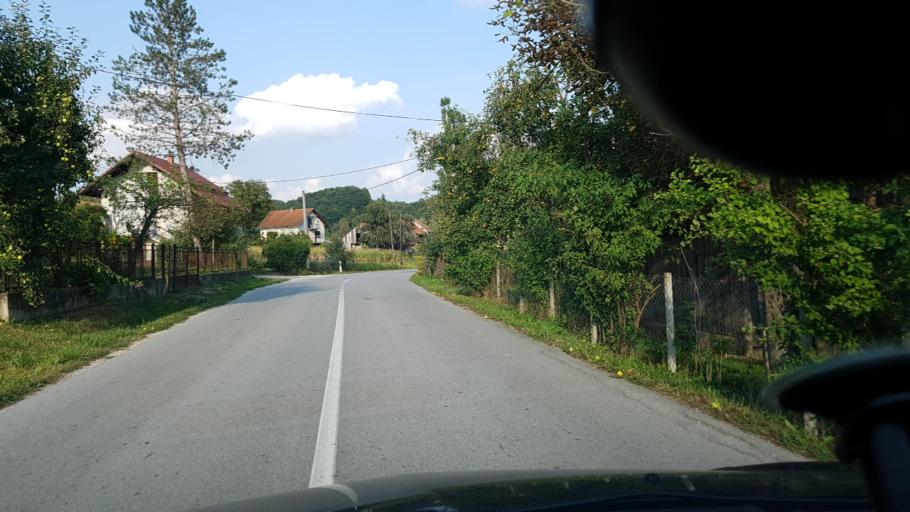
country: HR
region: Krapinsko-Zagorska
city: Pregrada
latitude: 46.1520
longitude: 15.6947
